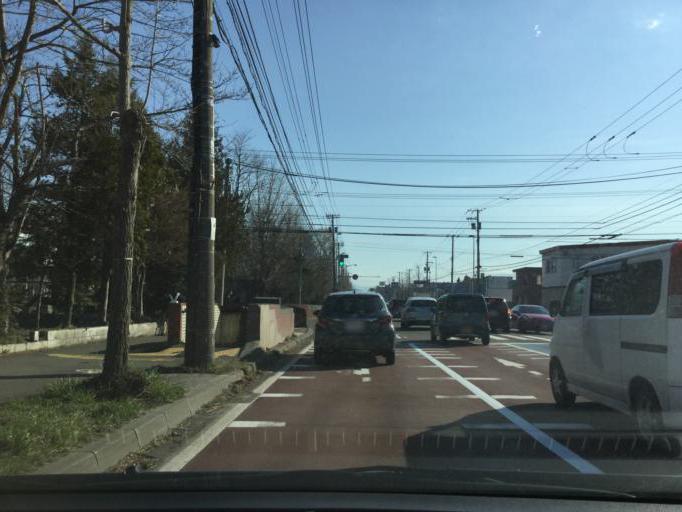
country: JP
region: Hokkaido
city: Iwamizawa
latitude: 43.1953
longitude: 141.7670
